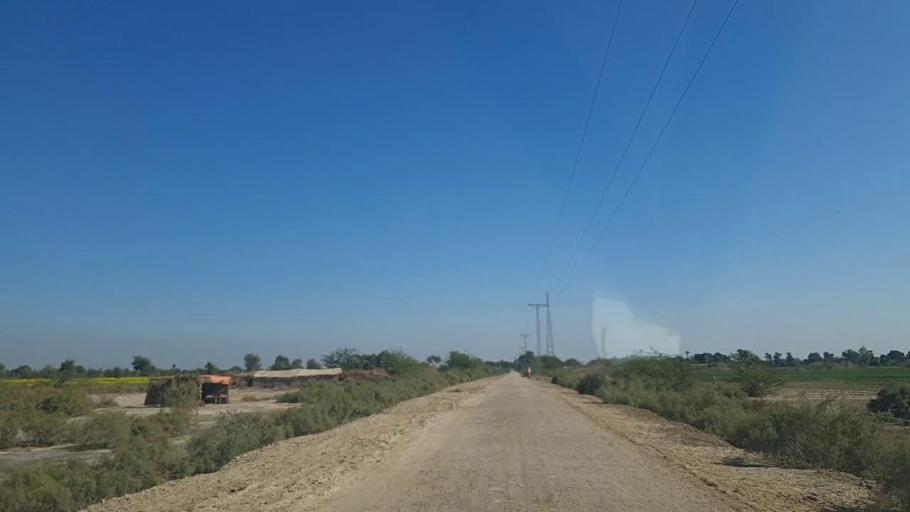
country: PK
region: Sindh
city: Khadro
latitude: 26.1774
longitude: 68.8232
